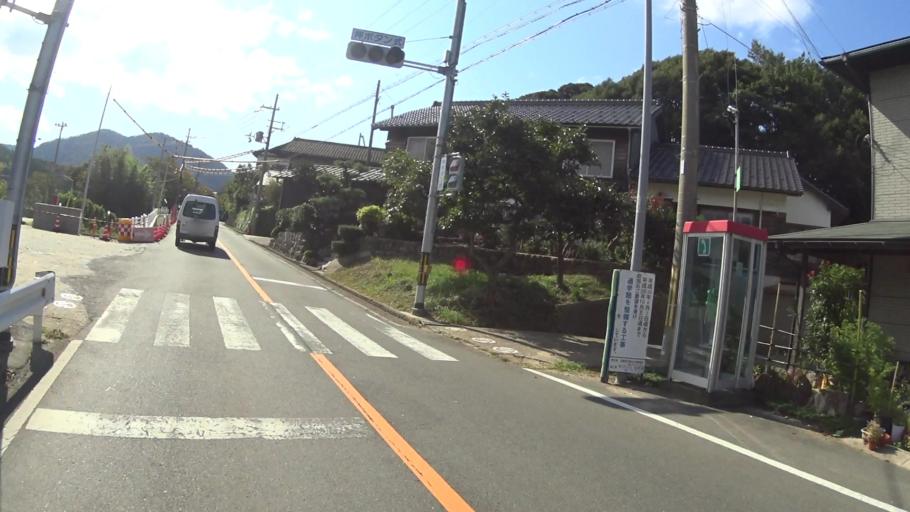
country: JP
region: Kyoto
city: Miyazu
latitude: 35.7529
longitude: 135.1723
